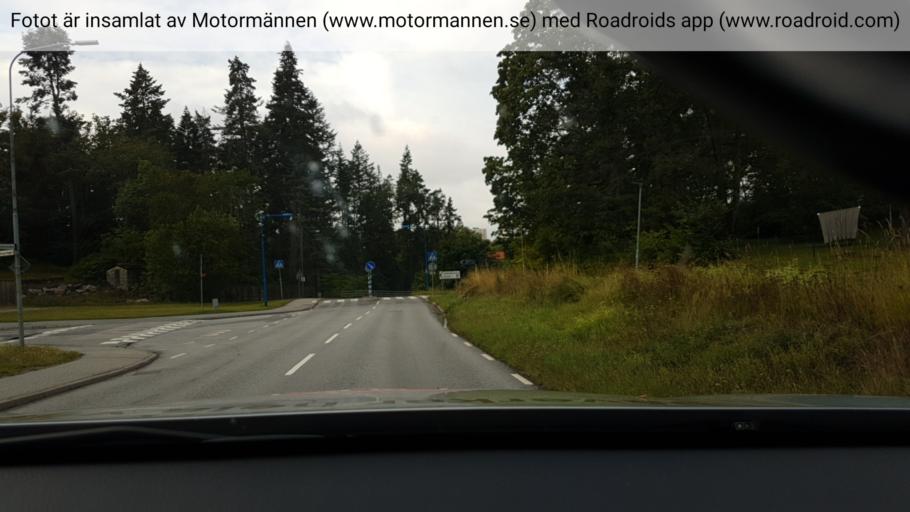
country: SE
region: Stockholm
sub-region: Danderyds Kommun
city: Djursholm
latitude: 59.3829
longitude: 18.0550
